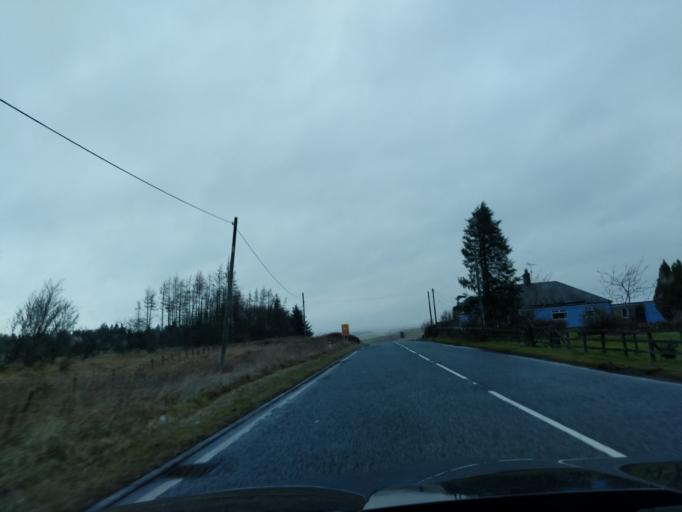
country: GB
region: England
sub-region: Northumberland
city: Otterburn
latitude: 55.2091
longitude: -2.1048
